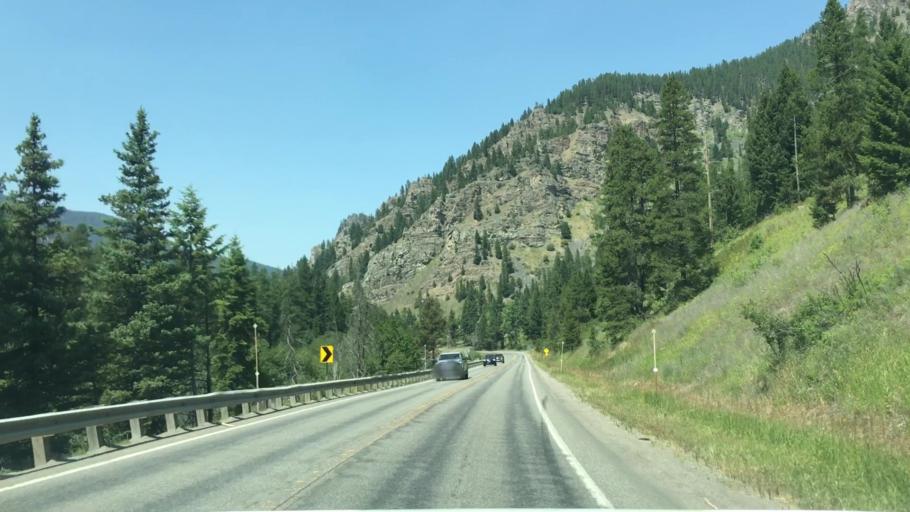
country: US
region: Montana
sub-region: Gallatin County
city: Big Sky
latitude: 45.3916
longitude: -111.2046
